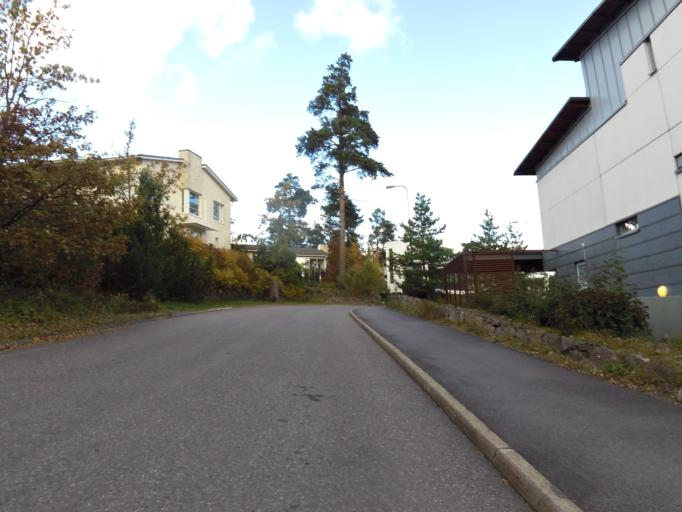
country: FI
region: Uusimaa
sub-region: Helsinki
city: Koukkuniemi
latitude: 60.1456
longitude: 24.7372
